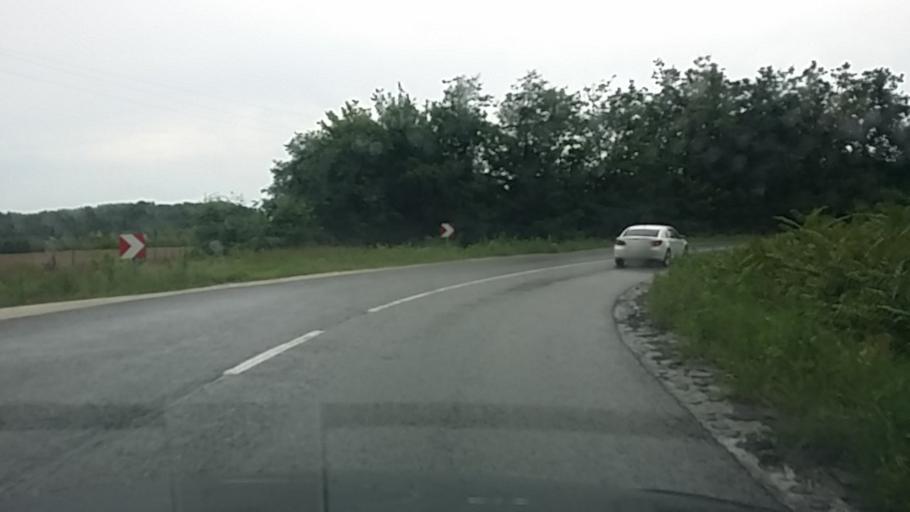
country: HU
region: Pest
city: Vecses
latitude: 47.3498
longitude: 19.3073
